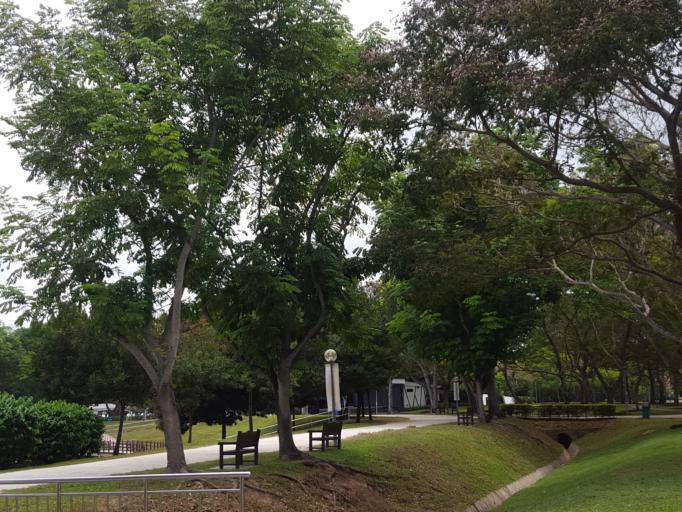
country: SG
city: Singapore
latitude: 1.3383
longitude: 103.9330
